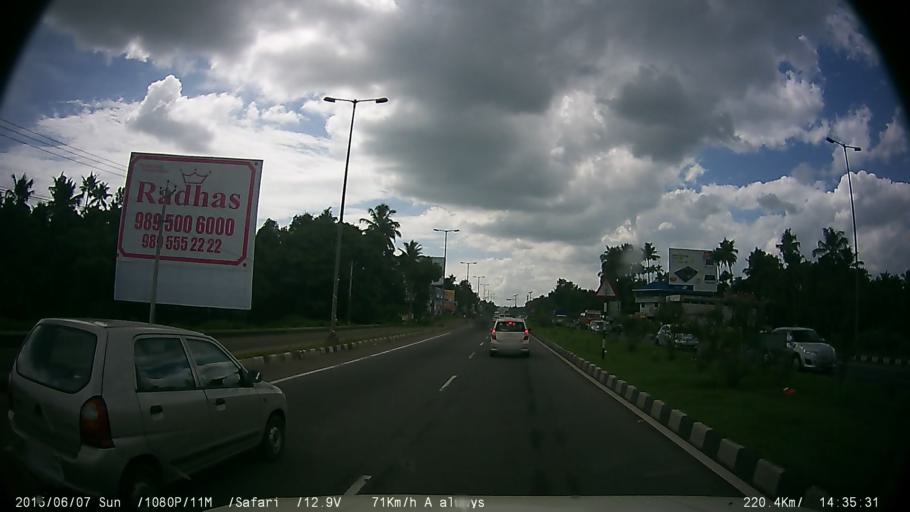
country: IN
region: Kerala
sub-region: Thrissur District
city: Kizhake Chalakudi
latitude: 10.3175
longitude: 76.3276
